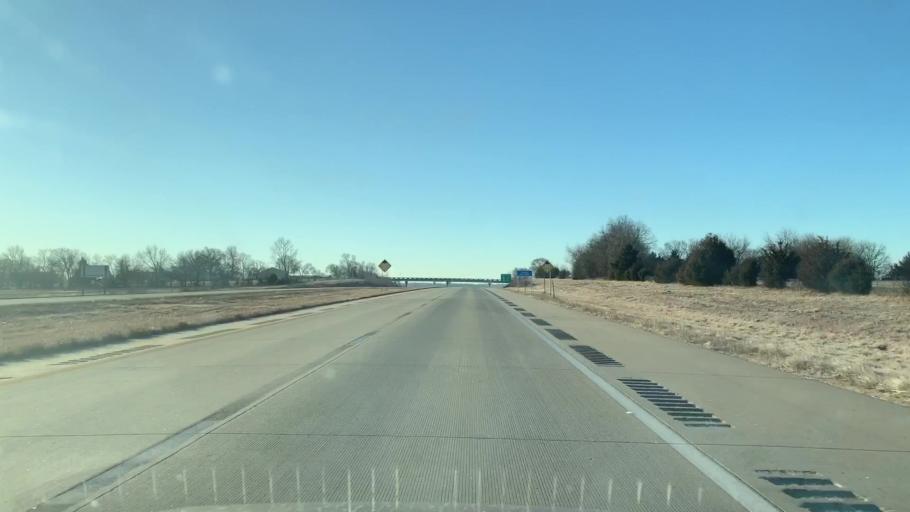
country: US
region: Kansas
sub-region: Bourbon County
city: Fort Scott
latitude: 37.8675
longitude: -94.7044
